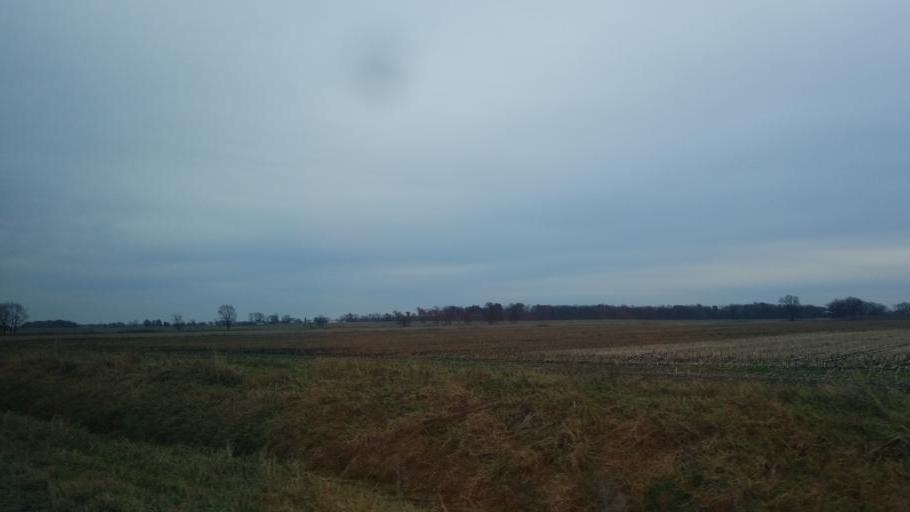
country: US
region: Indiana
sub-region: Adams County
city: Berne
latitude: 40.6735
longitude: -84.8711
